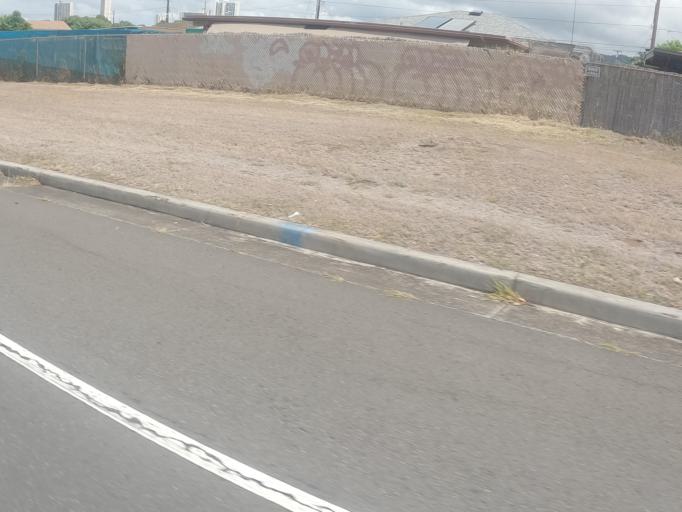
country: US
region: Hawaii
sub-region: Honolulu County
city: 'Aiea
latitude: 21.3762
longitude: -157.9323
